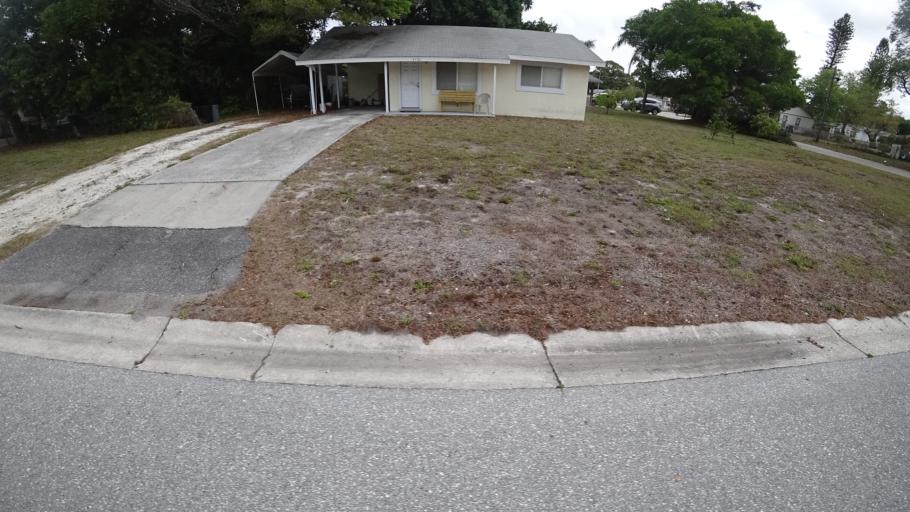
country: US
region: Florida
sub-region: Manatee County
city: South Bradenton
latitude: 27.4562
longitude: -82.5833
